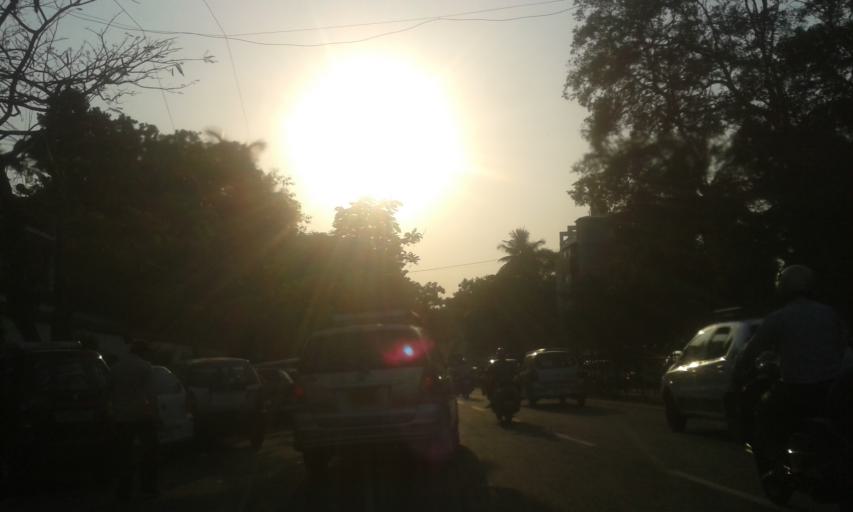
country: IN
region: Karnataka
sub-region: Bangalore Urban
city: Bangalore
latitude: 12.9482
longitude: 77.5714
